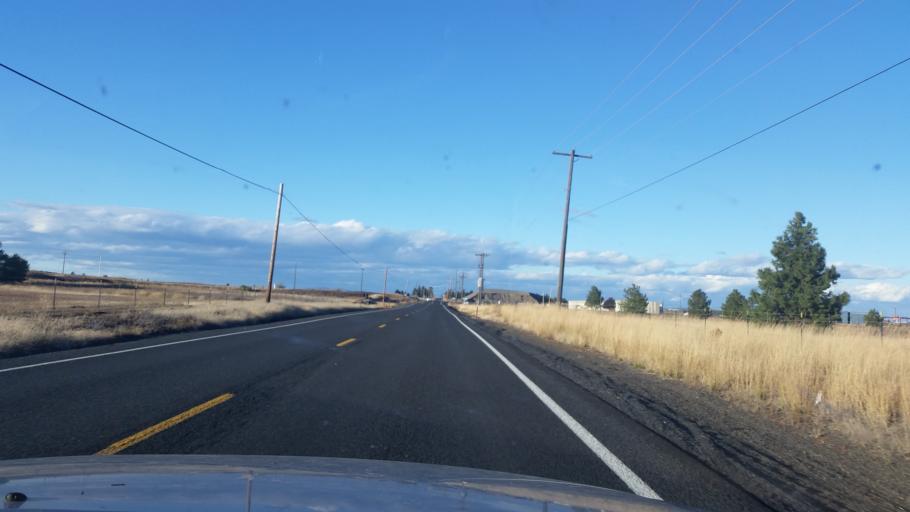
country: US
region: Washington
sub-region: Spokane County
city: Airway Heights
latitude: 47.6250
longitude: -117.6040
